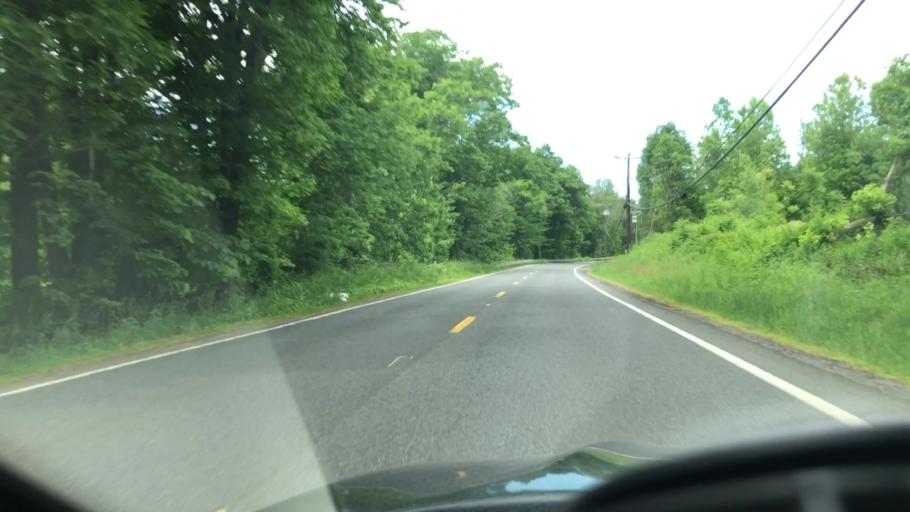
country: US
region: Massachusetts
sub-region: Hampshire County
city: Westhampton
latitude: 42.2519
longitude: -72.8673
